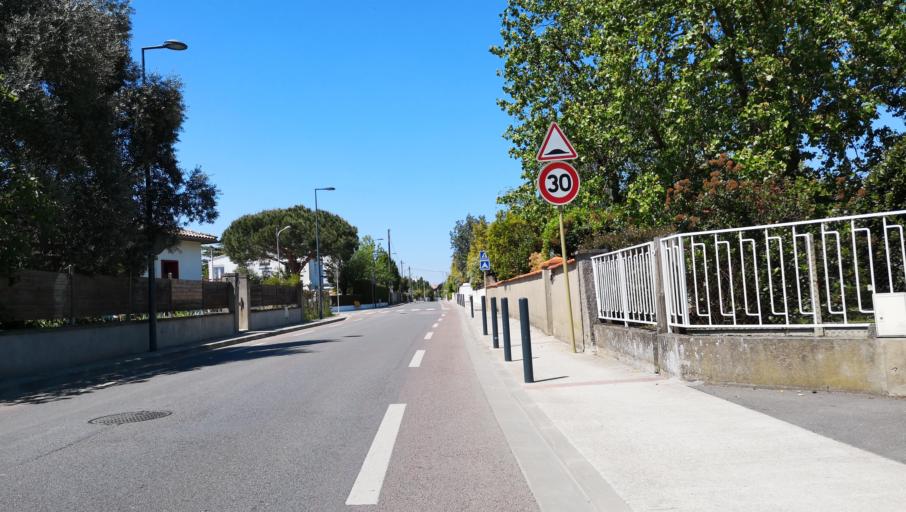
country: FR
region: Midi-Pyrenees
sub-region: Departement de la Haute-Garonne
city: Blagnac
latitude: 43.6415
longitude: 1.3910
